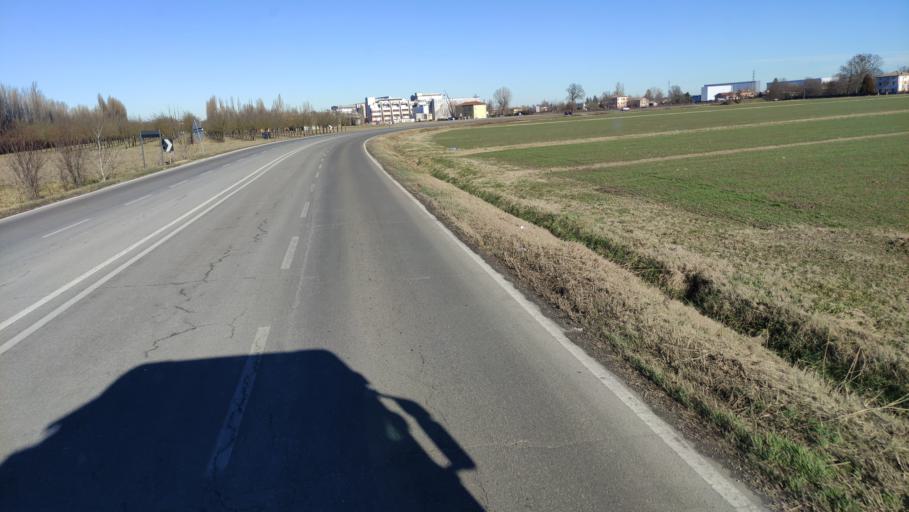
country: IT
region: Emilia-Romagna
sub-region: Provincia di Reggio Emilia
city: Correggio
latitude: 44.7599
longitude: 10.7945
